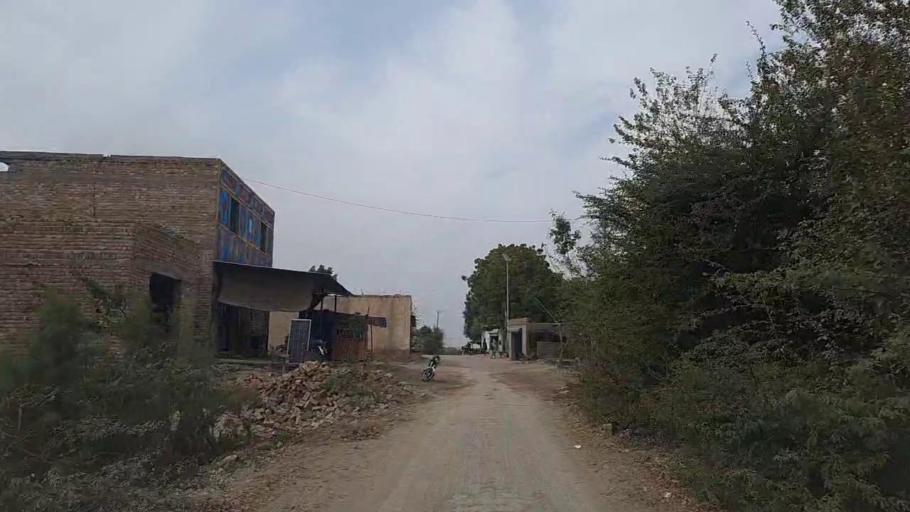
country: PK
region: Sindh
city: Daur
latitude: 26.4476
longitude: 68.4511
